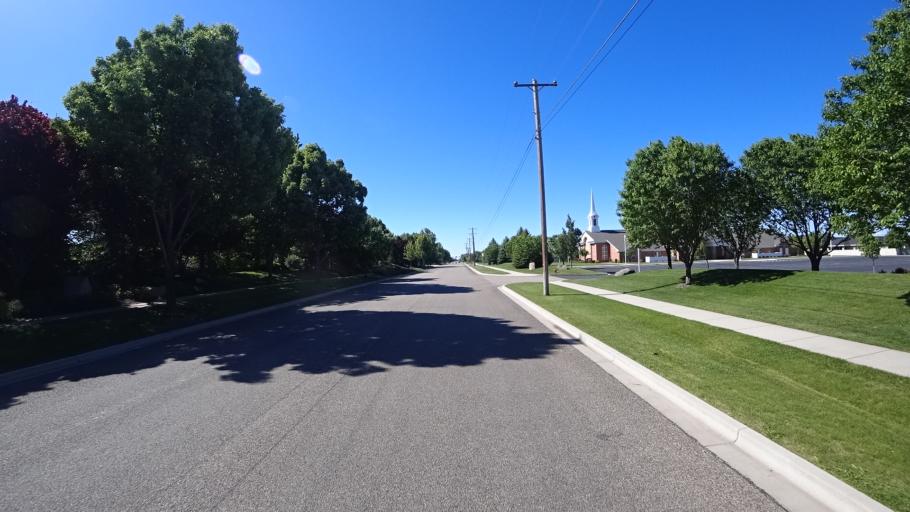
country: US
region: Idaho
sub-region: Ada County
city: Eagle
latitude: 43.6660
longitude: -116.3936
